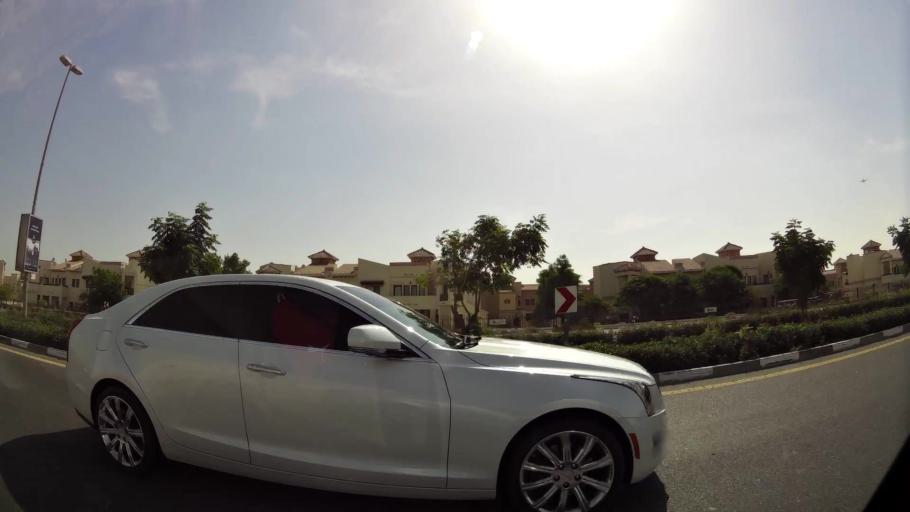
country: AE
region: Ash Shariqah
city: Sharjah
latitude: 25.2171
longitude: 55.4270
